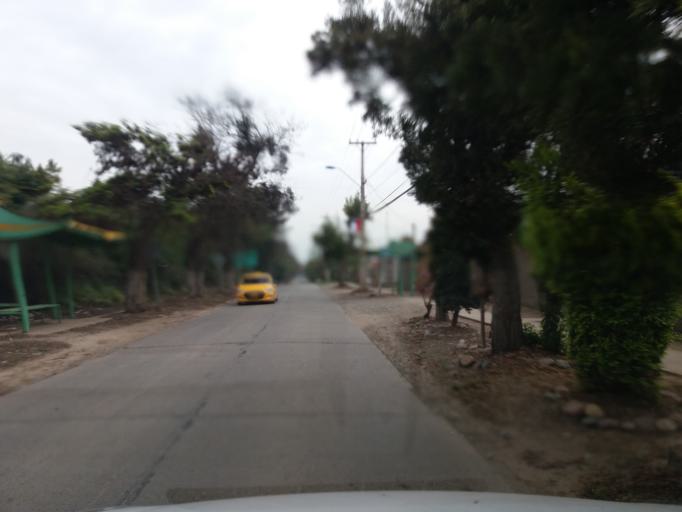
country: CL
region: Valparaiso
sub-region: Provincia de Quillota
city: Hacienda La Calera
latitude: -32.8170
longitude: -71.1361
